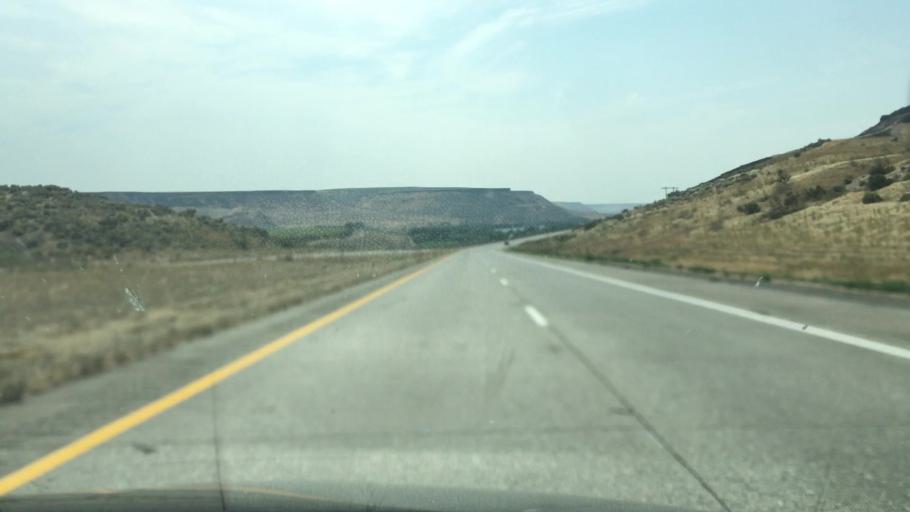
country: US
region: Idaho
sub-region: Elmore County
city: Glenns Ferry
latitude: 42.9595
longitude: -115.3445
